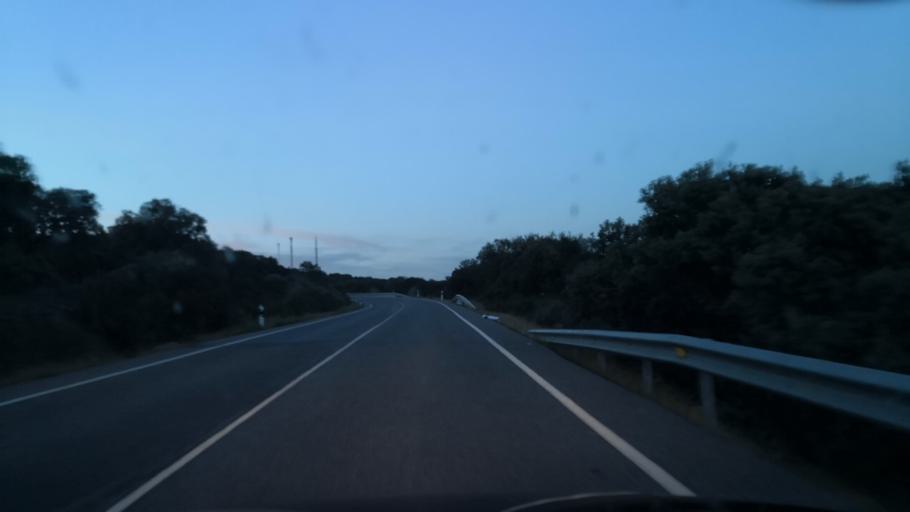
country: ES
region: Extremadura
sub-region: Provincia de Caceres
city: Alcantara
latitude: 39.7415
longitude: -6.9023
